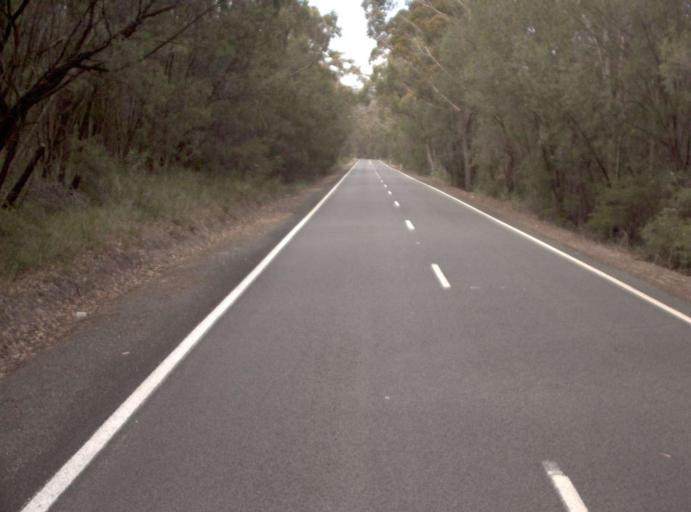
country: AU
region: New South Wales
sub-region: Bega Valley
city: Eden
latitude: -37.4963
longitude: 149.5473
